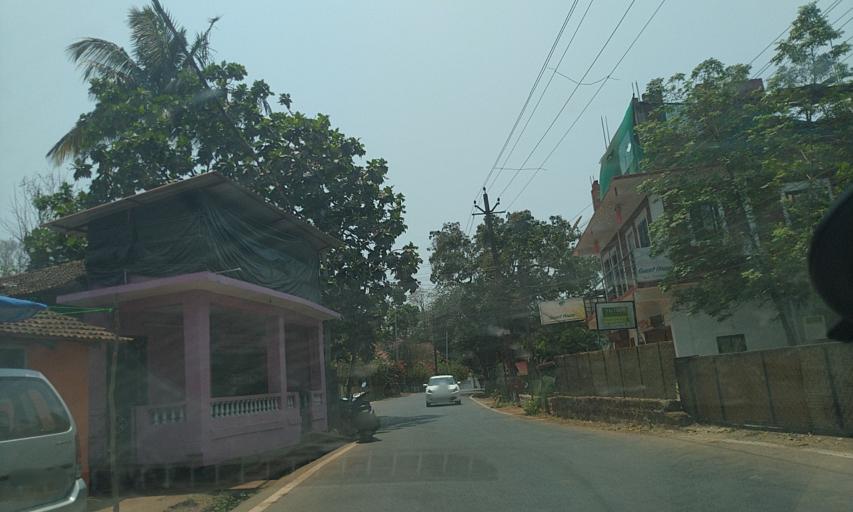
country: IN
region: Goa
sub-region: North Goa
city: Solim
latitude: 15.5957
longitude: 73.7789
